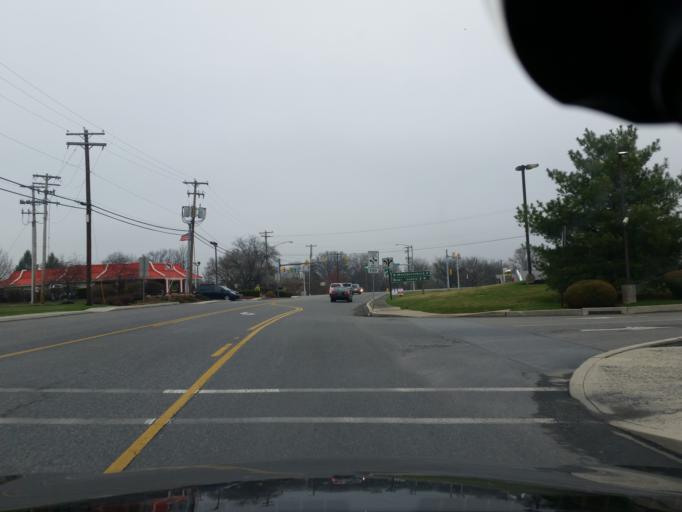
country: US
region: Pennsylvania
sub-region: Cumberland County
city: Mechanicsburg
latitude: 40.1752
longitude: -76.9857
